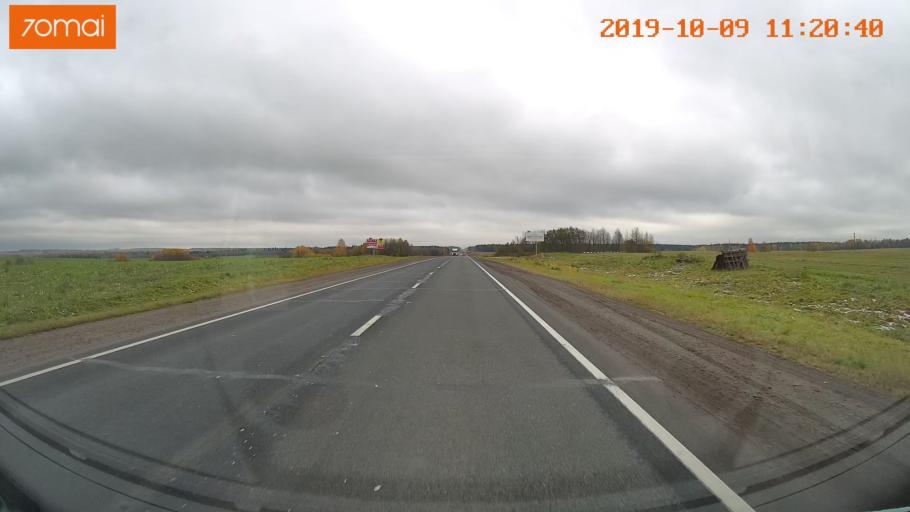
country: RU
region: Vologda
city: Vologda
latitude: 59.1471
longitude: 39.9412
